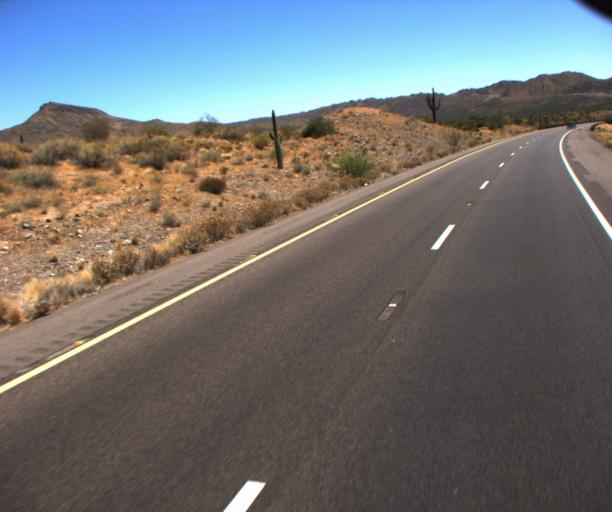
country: US
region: Arizona
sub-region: Maricopa County
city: Rio Verde
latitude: 33.7413
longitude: -111.5040
